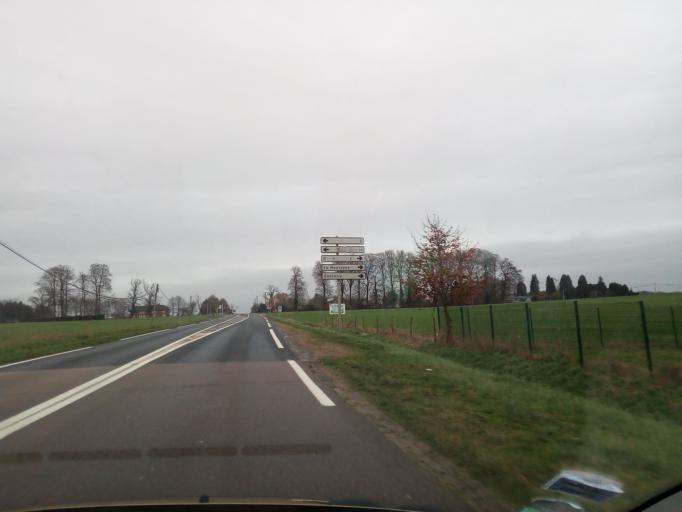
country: FR
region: Haute-Normandie
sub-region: Departement de l'Eure
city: Hauville
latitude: 49.3864
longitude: 0.7988
